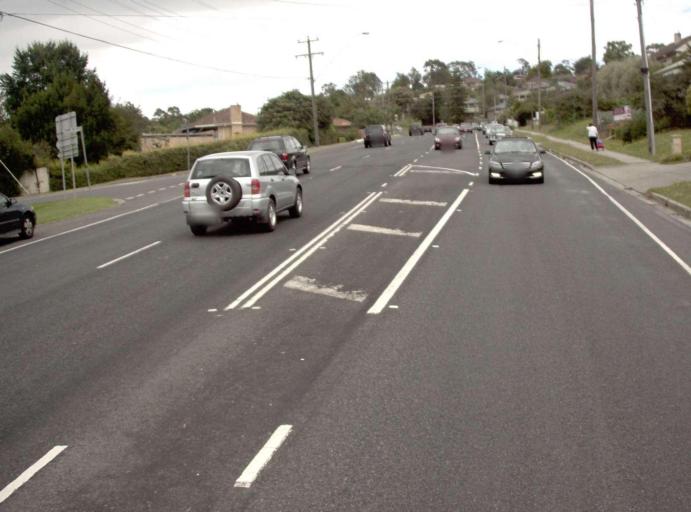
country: AU
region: Victoria
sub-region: Yarra Ranges
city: Lilydale
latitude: -37.7568
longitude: 145.3417
